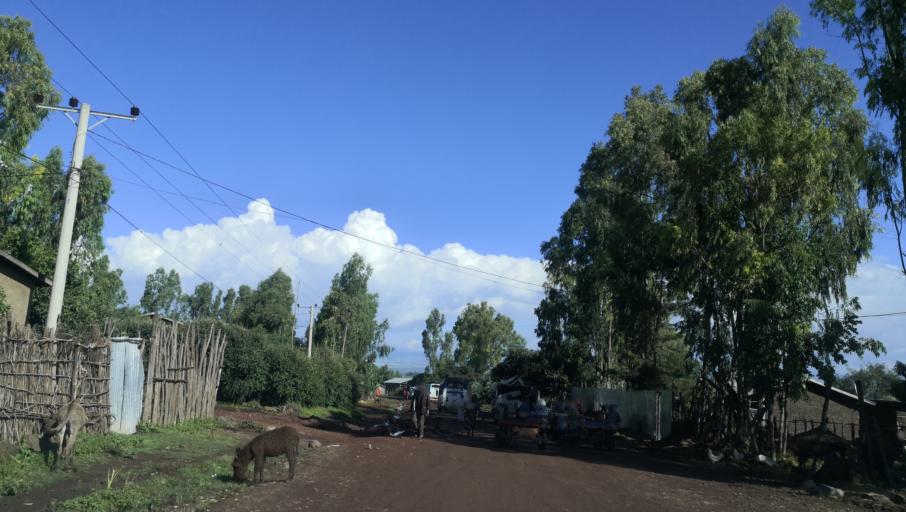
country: ET
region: Oromiya
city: Tulu Bolo
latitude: 8.6438
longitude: 38.2224
